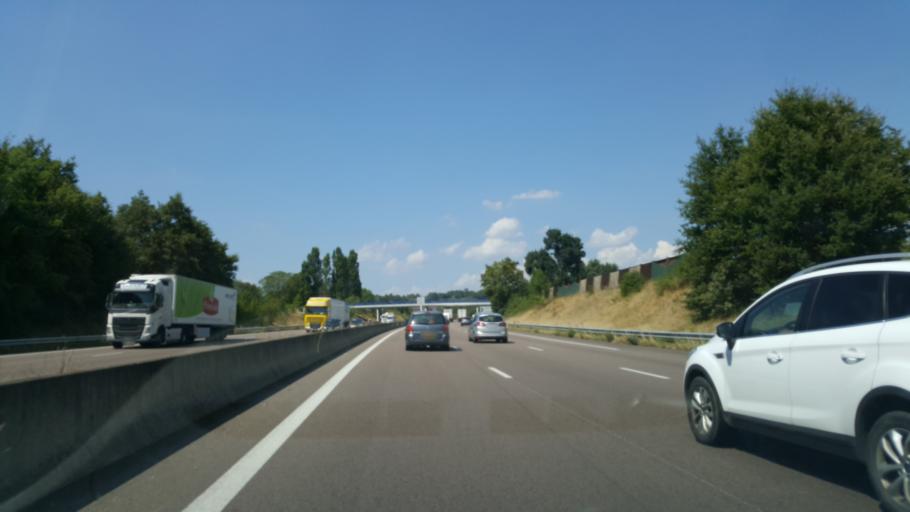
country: FR
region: Bourgogne
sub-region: Departement de Saone-et-Loire
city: Tournus
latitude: 46.5583
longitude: 4.8988
